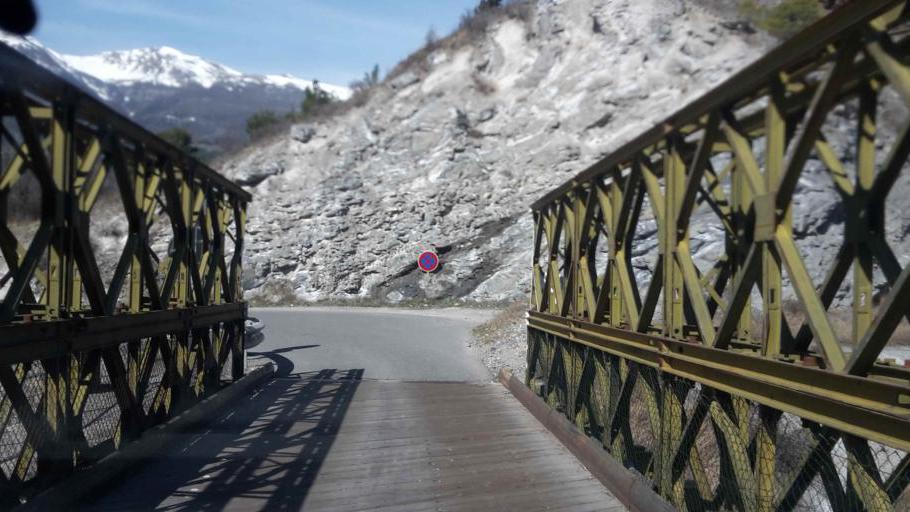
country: FR
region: Provence-Alpes-Cote d'Azur
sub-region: Departement des Hautes-Alpes
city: Embrun
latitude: 44.5611
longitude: 6.5123
